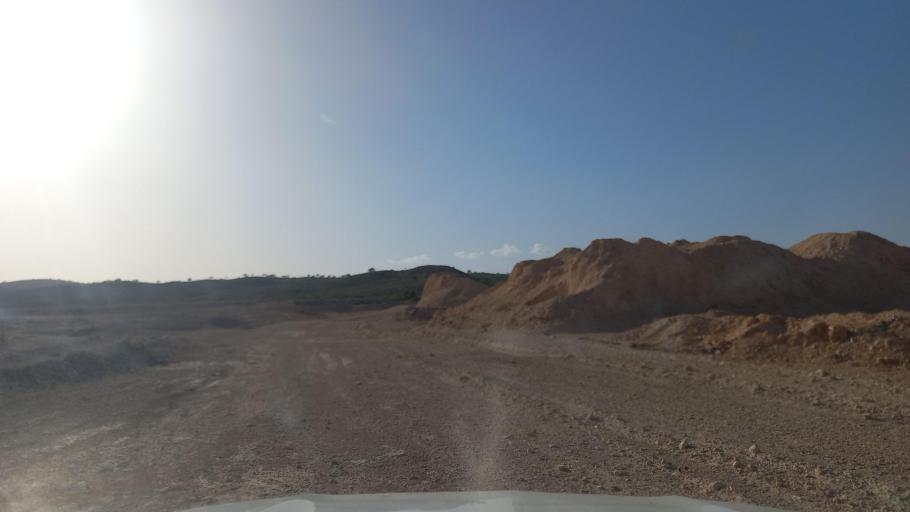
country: TN
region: Al Qasrayn
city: Sbiba
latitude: 35.3651
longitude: 8.9971
